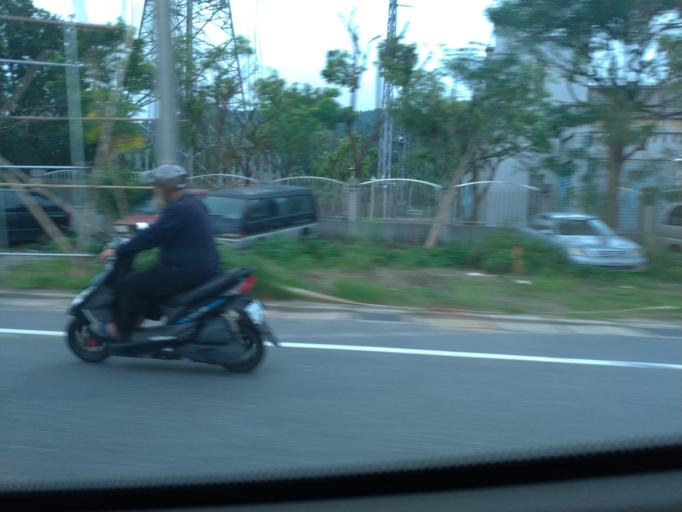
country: TW
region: Taiwan
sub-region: Taoyuan
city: Taoyuan
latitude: 24.9315
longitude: 121.3849
